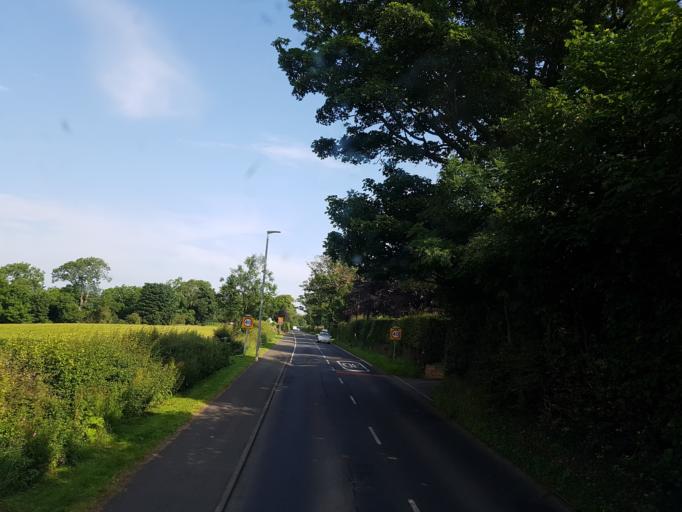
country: GB
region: England
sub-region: Northumberland
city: Alnmouth
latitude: 55.3998
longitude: -1.6355
